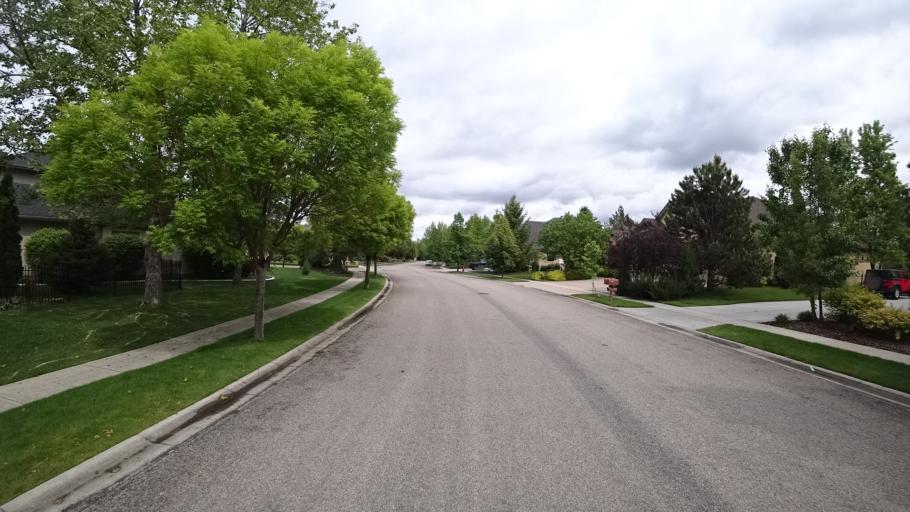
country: US
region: Idaho
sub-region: Ada County
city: Eagle
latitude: 43.6800
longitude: -116.3619
